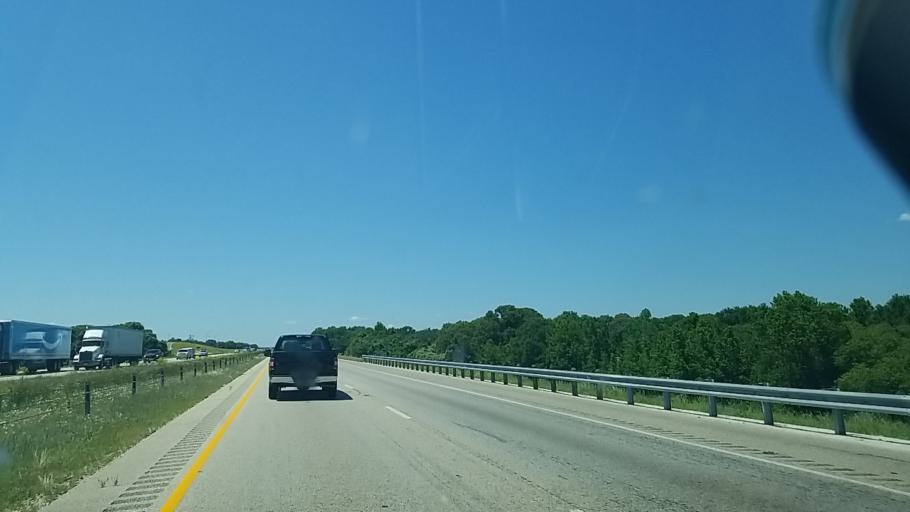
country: US
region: Texas
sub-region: Leon County
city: Buffalo
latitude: 31.4315
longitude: -96.0583
